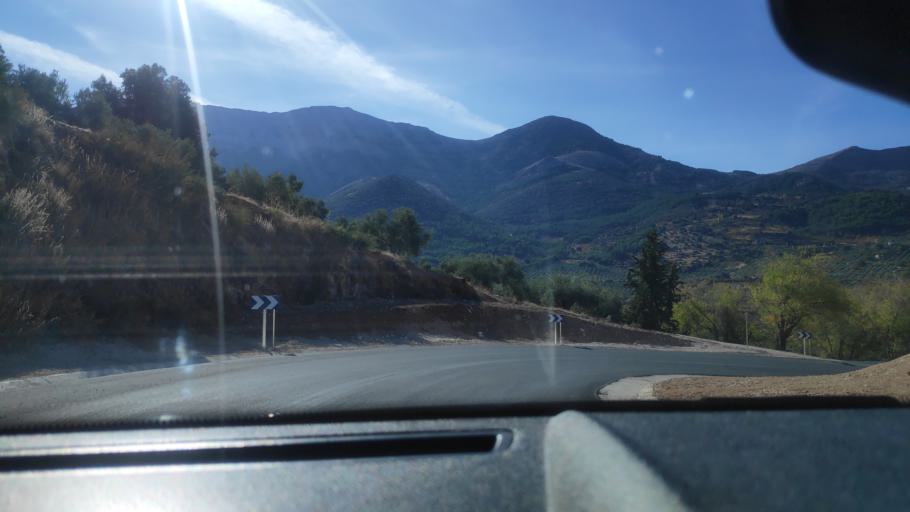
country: ES
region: Andalusia
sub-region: Provincia de Jaen
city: Torres
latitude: 37.7743
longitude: -3.4976
